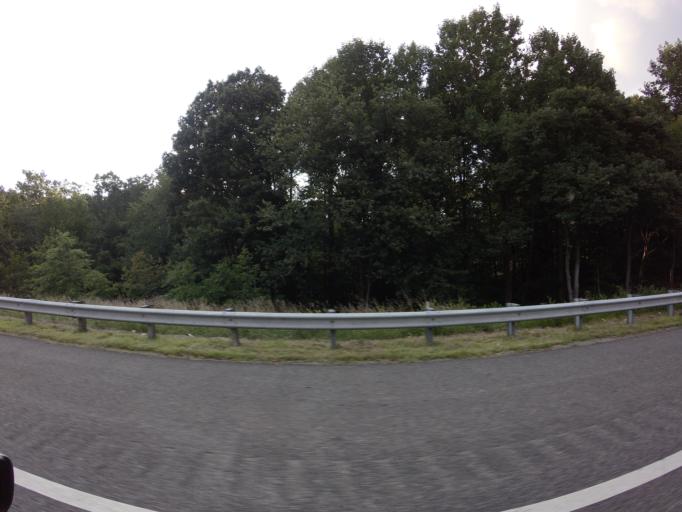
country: US
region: Maryland
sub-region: Prince George's County
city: West Laurel
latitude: 39.1104
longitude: -76.8796
